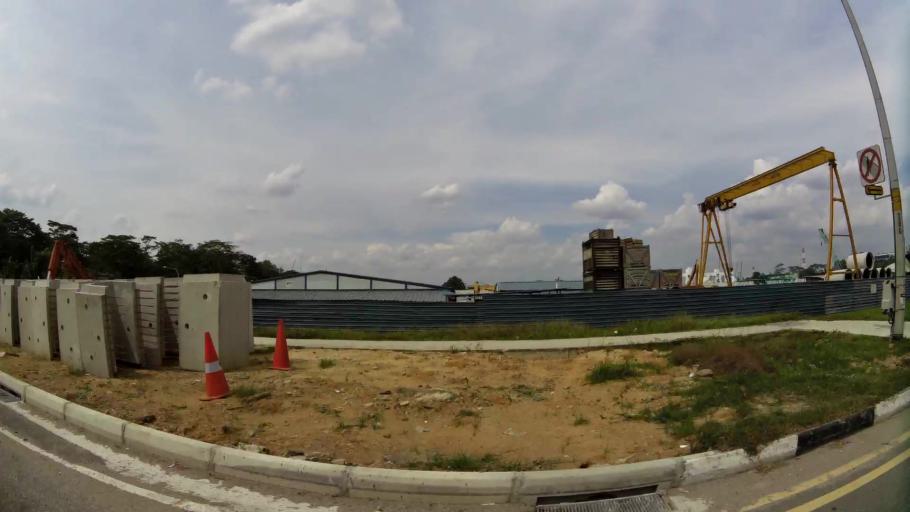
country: MY
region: Johor
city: Johor Bahru
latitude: 1.4239
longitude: 103.7579
